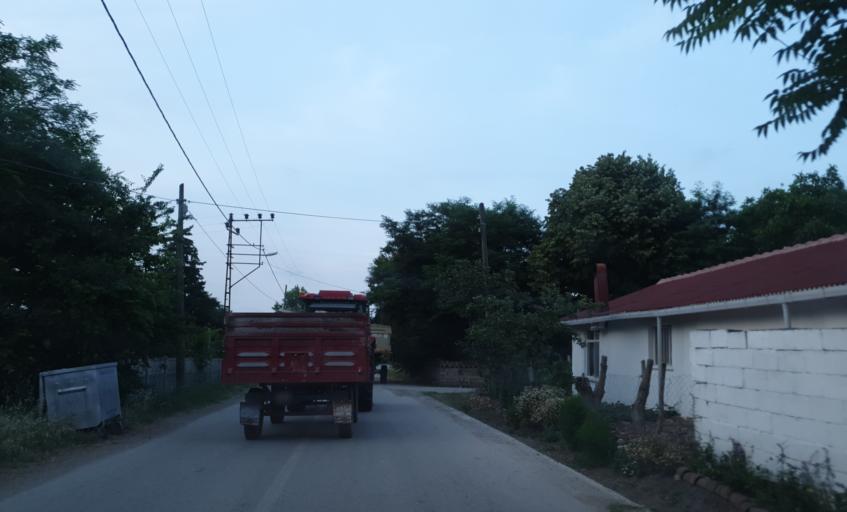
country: TR
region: Tekirdag
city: Beyazkoy
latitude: 41.4116
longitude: 27.6540
